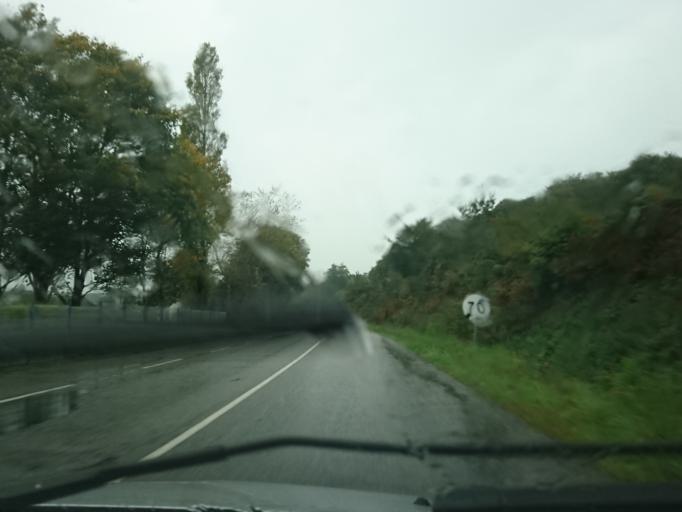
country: FR
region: Brittany
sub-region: Departement du Finistere
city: Plouvien
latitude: 48.5414
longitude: -4.4907
